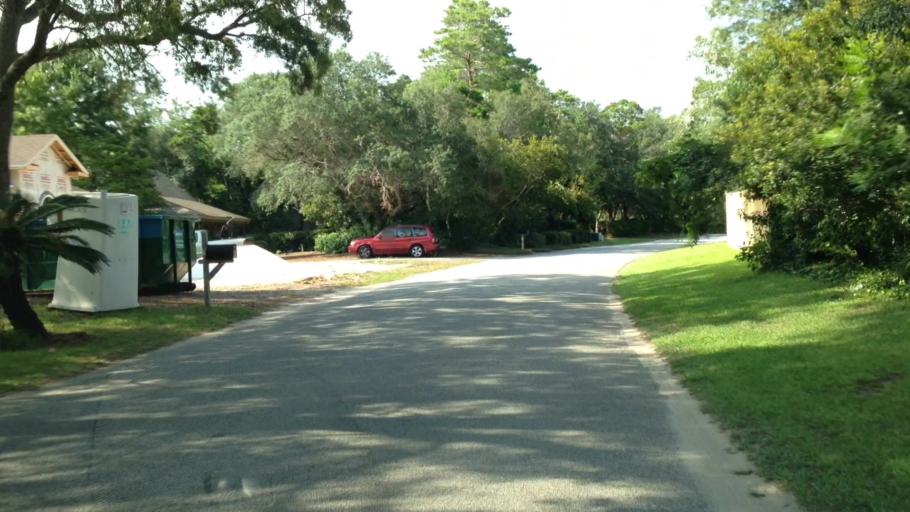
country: US
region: Florida
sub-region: Santa Rosa County
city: Holley
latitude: 30.4414
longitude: -86.9350
